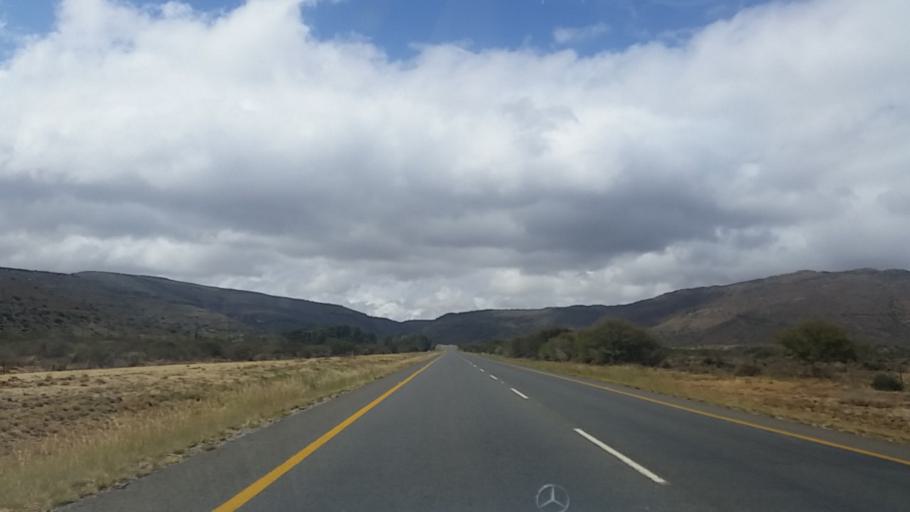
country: ZA
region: Eastern Cape
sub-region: Cacadu District Municipality
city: Graaff-Reinet
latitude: -31.9843
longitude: 24.6943
